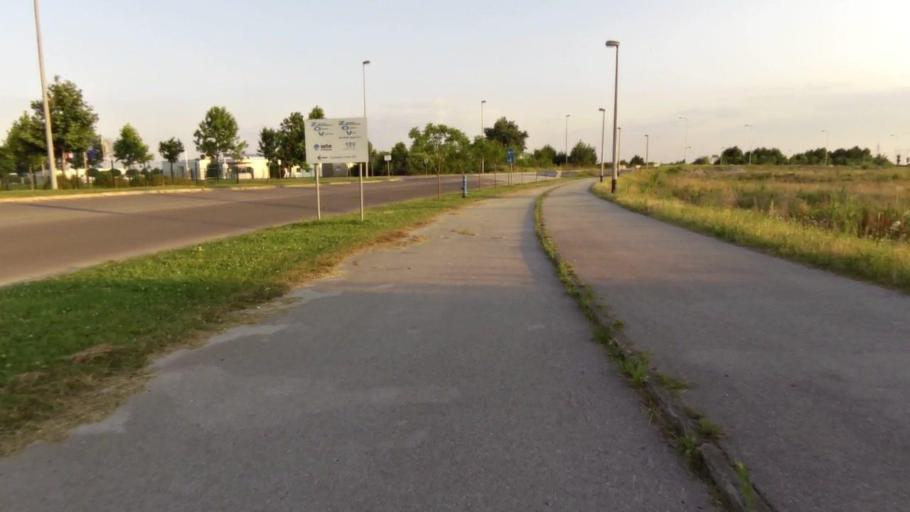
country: HR
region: Zagrebacka
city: Micevec
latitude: 45.7884
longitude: 16.0790
